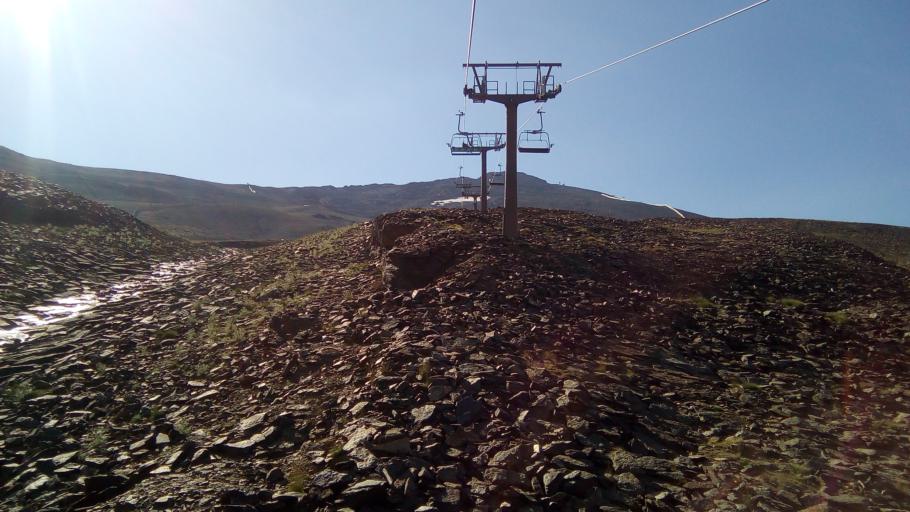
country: ES
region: Andalusia
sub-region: Provincia de Granada
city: Guejar-Sierra
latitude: 37.0679
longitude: -3.3823
